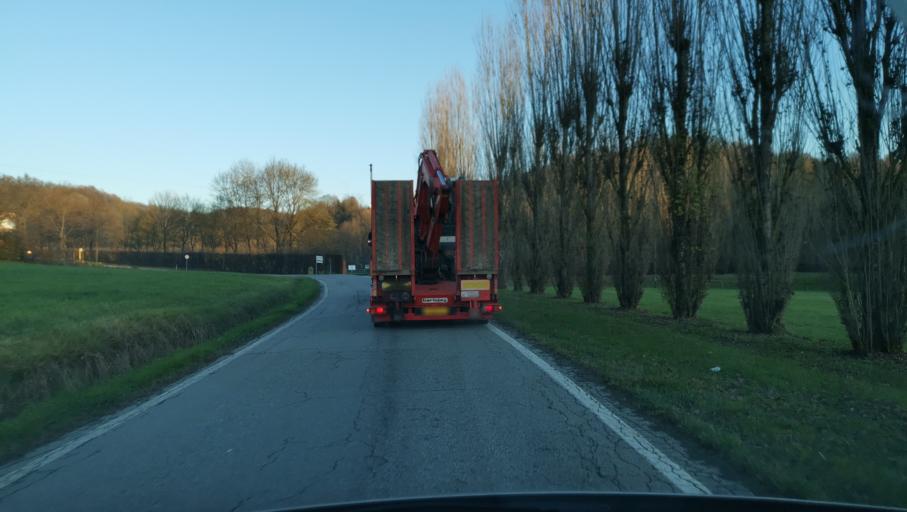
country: IT
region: Piedmont
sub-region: Provincia di Torino
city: Rivalba
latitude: 45.1088
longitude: 7.8939
